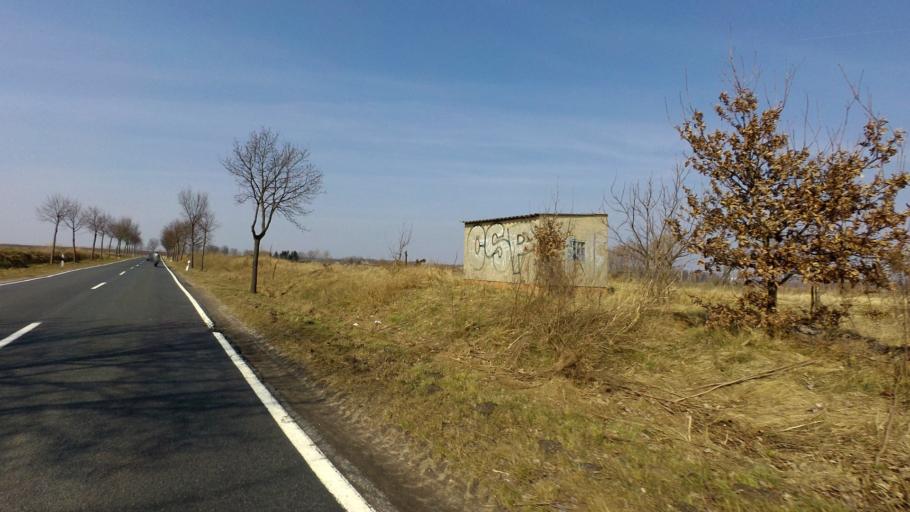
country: DE
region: Brandenburg
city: Ketzin
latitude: 52.4473
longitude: 12.8433
